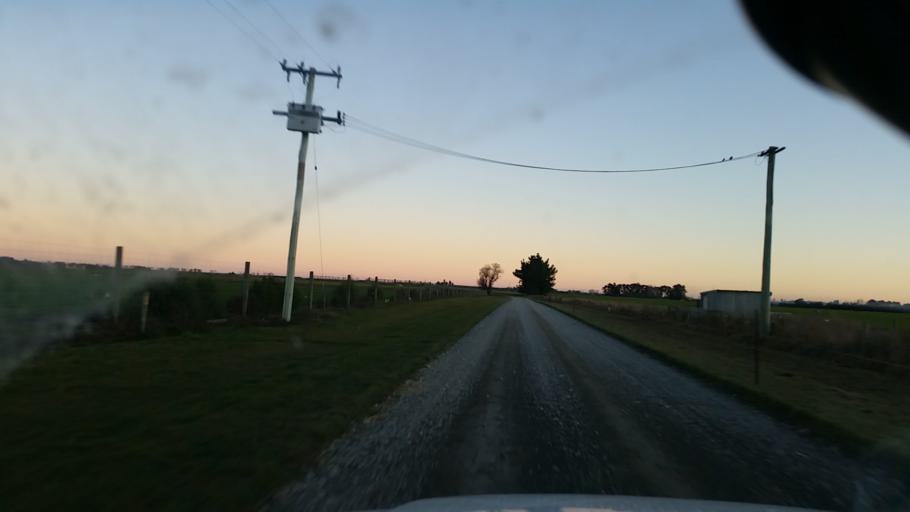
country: NZ
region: Canterbury
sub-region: Ashburton District
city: Tinwald
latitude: -44.0593
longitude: 171.6612
